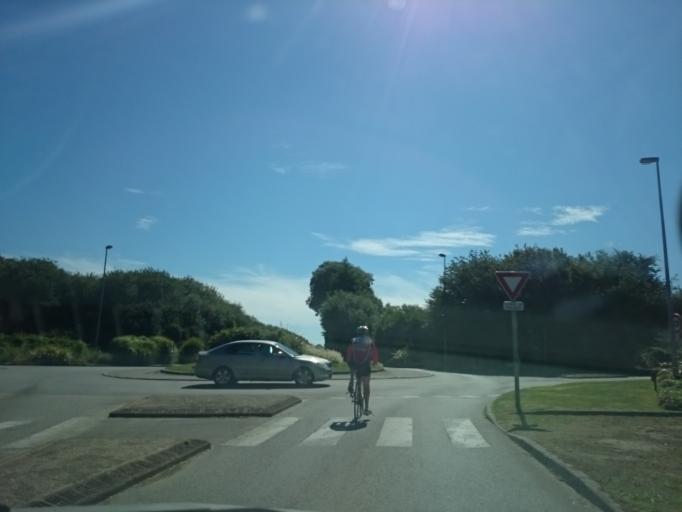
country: FR
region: Brittany
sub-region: Departement du Finistere
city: Saint-Renan
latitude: 48.4380
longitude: -4.6343
